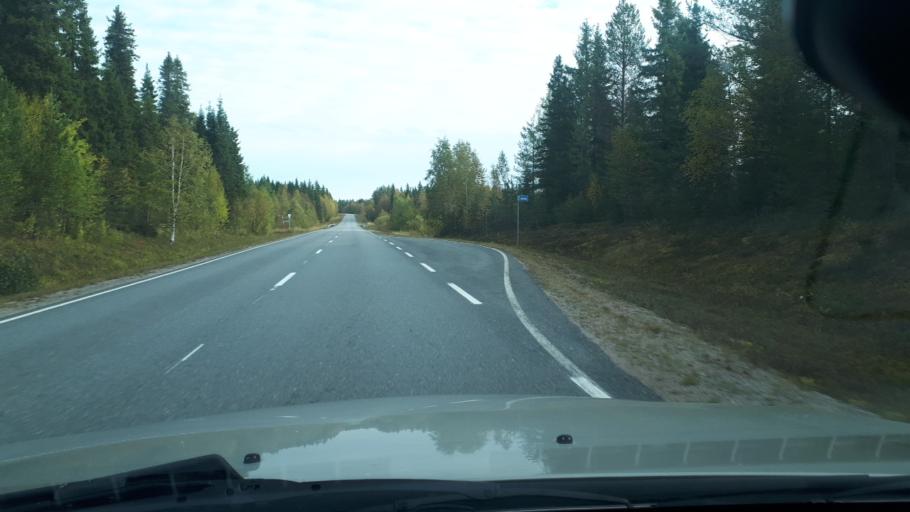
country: FI
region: Lapland
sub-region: Rovaniemi
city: Rovaniemi
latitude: 65.9552
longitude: 25.9310
